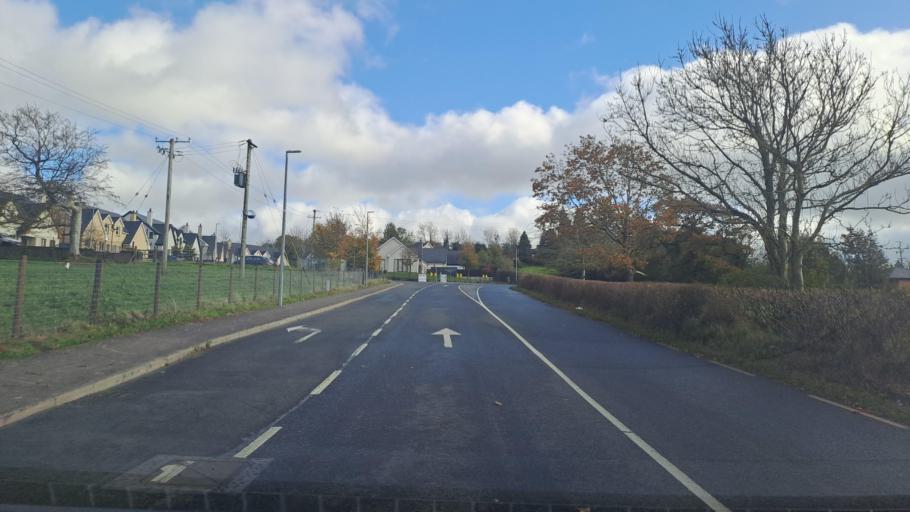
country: IE
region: Ulster
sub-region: County Monaghan
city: Monaghan
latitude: 54.1291
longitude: -6.9169
